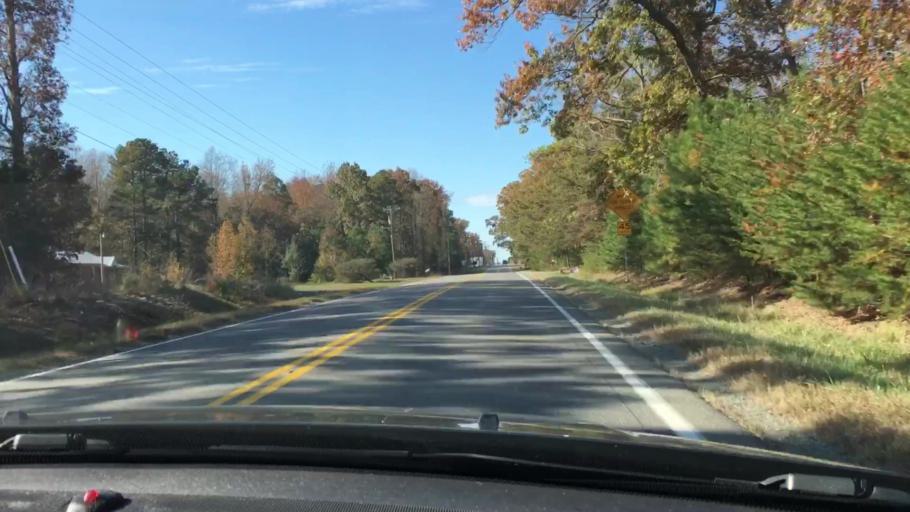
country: US
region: Virginia
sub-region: King William County
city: King William
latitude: 37.7160
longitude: -77.0689
